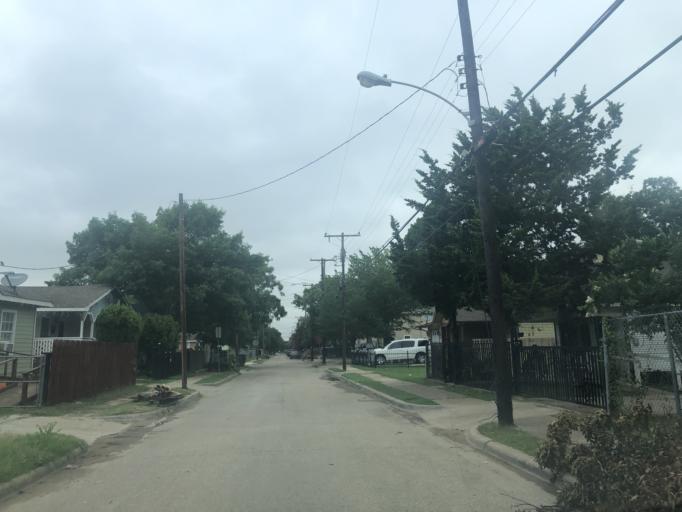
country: US
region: Texas
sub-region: Dallas County
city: Dallas
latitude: 32.7796
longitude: -96.8456
